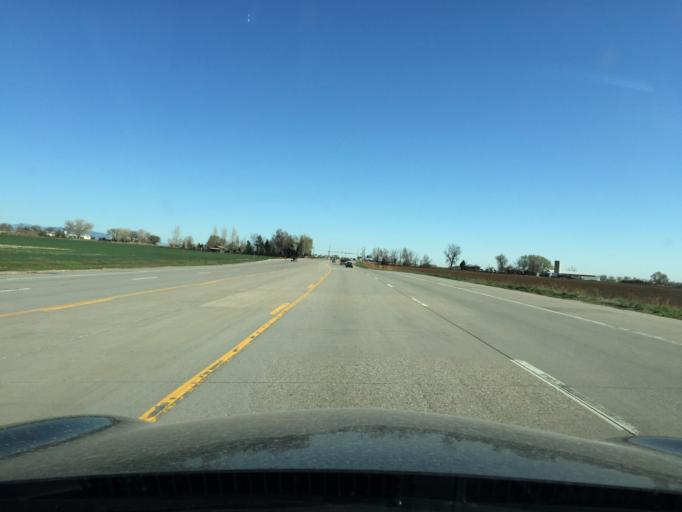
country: US
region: Colorado
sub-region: Boulder County
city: Erie
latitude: 40.0824
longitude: -105.1026
